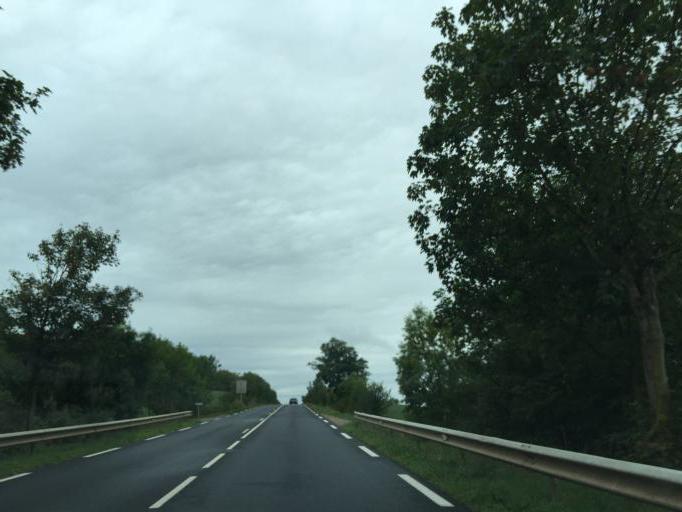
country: FR
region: Midi-Pyrenees
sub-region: Departement de l'Aveyron
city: Bozouls
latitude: 44.4821
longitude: 2.7349
